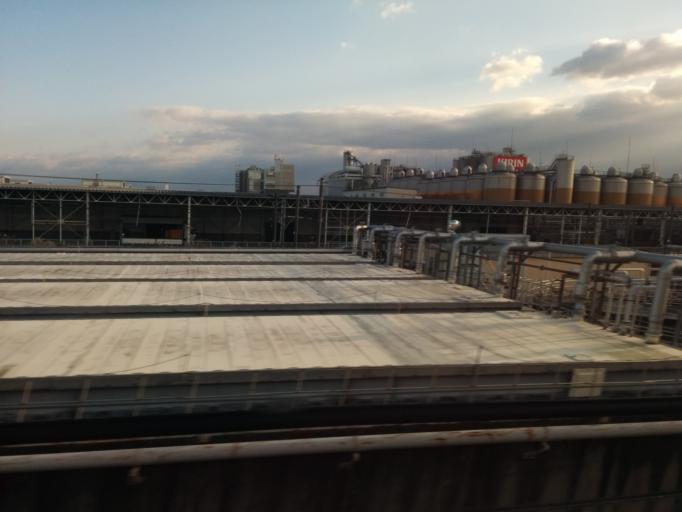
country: JP
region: Aichi
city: Nagoya-shi
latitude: 35.2081
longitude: 136.8490
